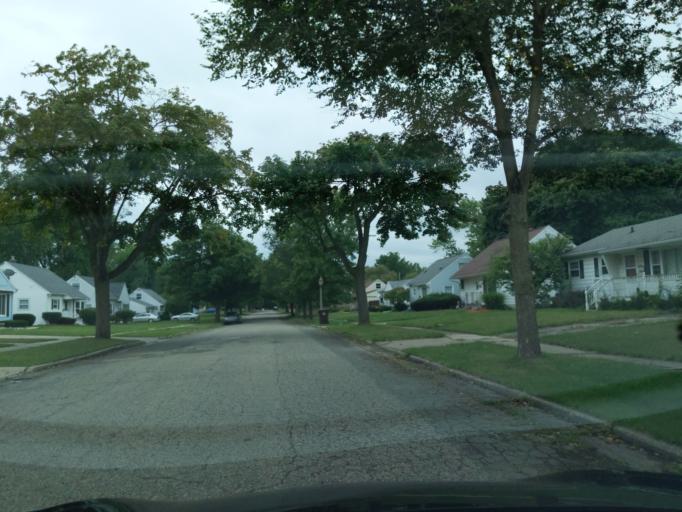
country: US
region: Michigan
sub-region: Ingham County
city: Lansing
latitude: 42.6895
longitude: -84.5368
